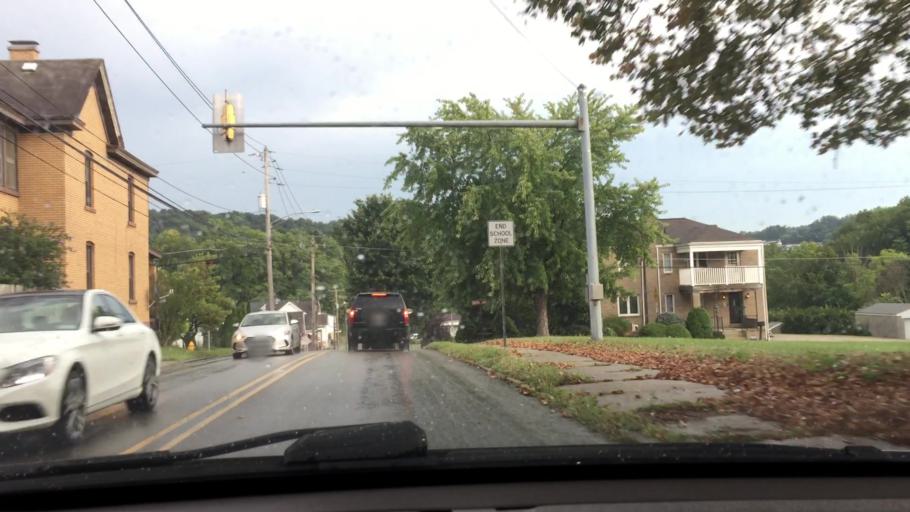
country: US
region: Pennsylvania
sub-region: Washington County
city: Canonsburg
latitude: 40.2671
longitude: -80.1800
